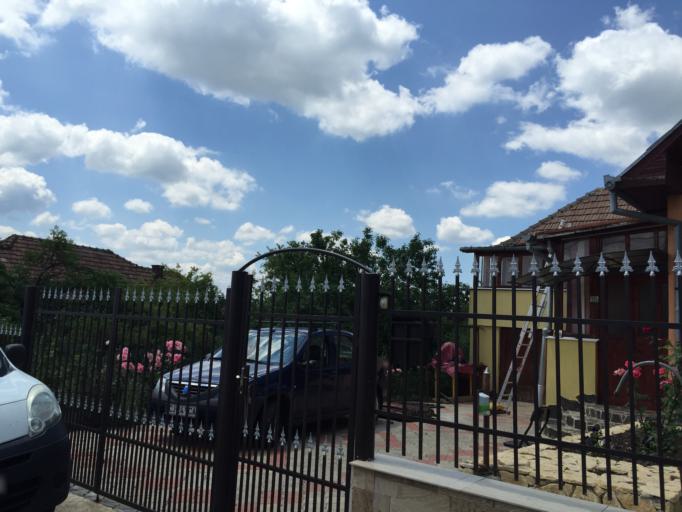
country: RO
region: Cluj
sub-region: Municipiul Cluj-Napoca
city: Cluj-Napoca
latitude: 46.7947
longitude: 23.5791
